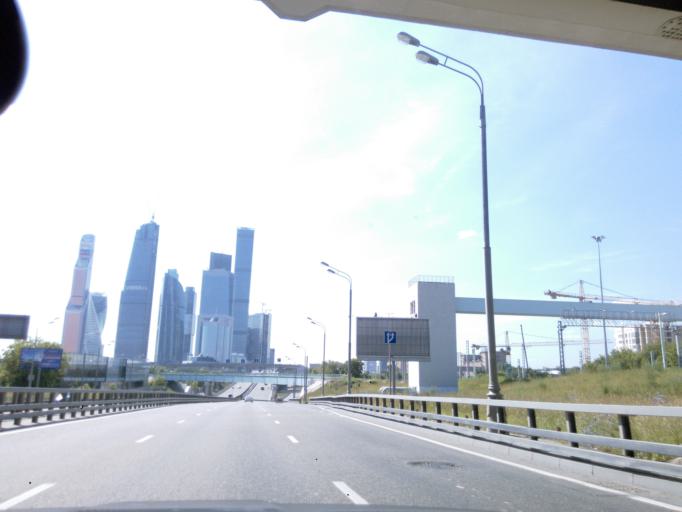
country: RU
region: Moskovskaya
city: Presnenskiy
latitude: 55.7600
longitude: 37.5244
